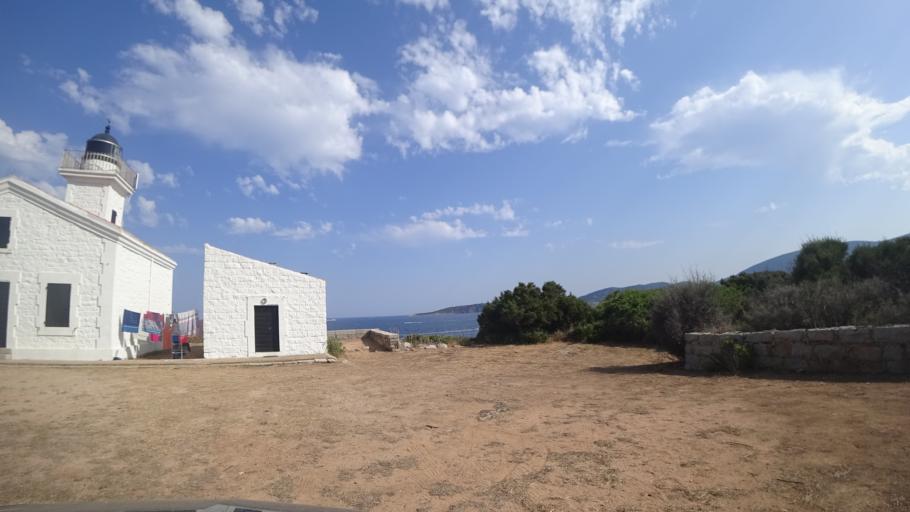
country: FR
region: Corsica
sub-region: Departement de la Corse-du-Sud
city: Porto-Vecchio
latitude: 41.6177
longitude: 9.3549
